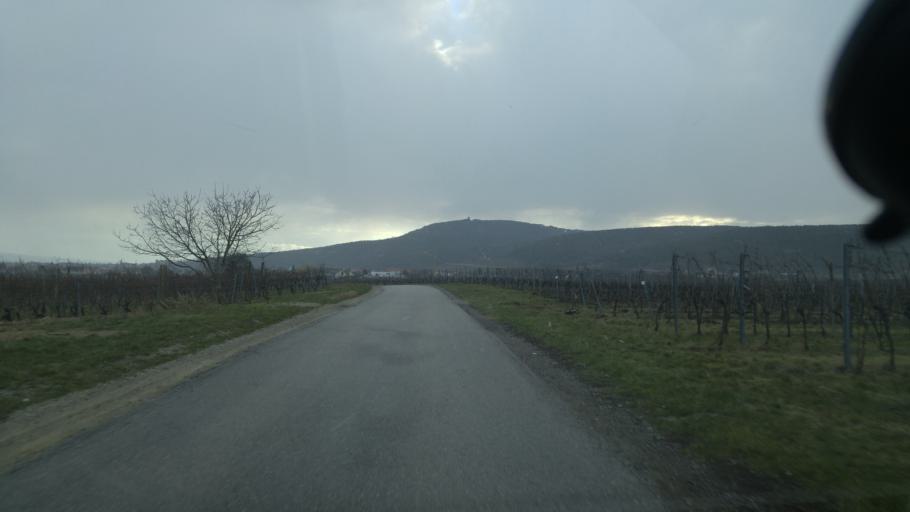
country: AT
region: Lower Austria
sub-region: Politischer Bezirk Baden
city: Bad Voslau
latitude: 47.9917
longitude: 16.2083
